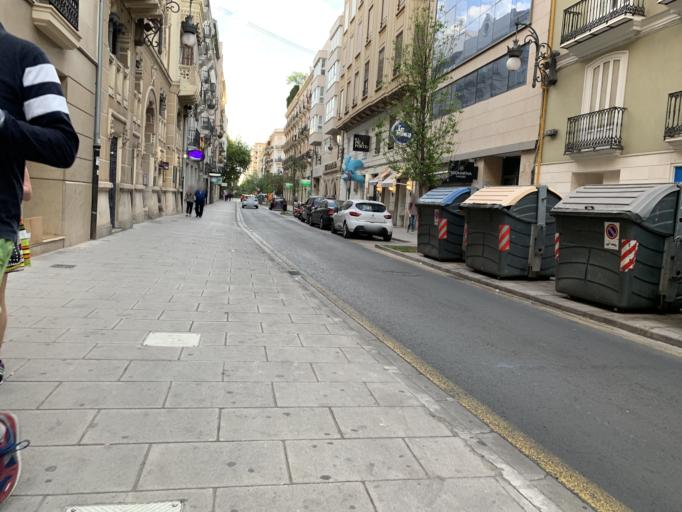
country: ES
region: Valencia
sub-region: Provincia de Valencia
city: Valencia
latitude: 39.4677
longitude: -0.3736
